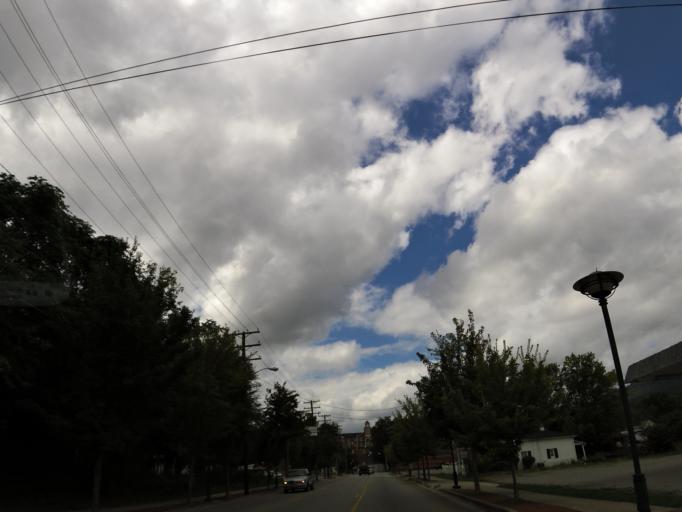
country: US
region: Tennessee
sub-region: Hamilton County
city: Lookout Mountain
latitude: 35.0096
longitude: -85.3173
